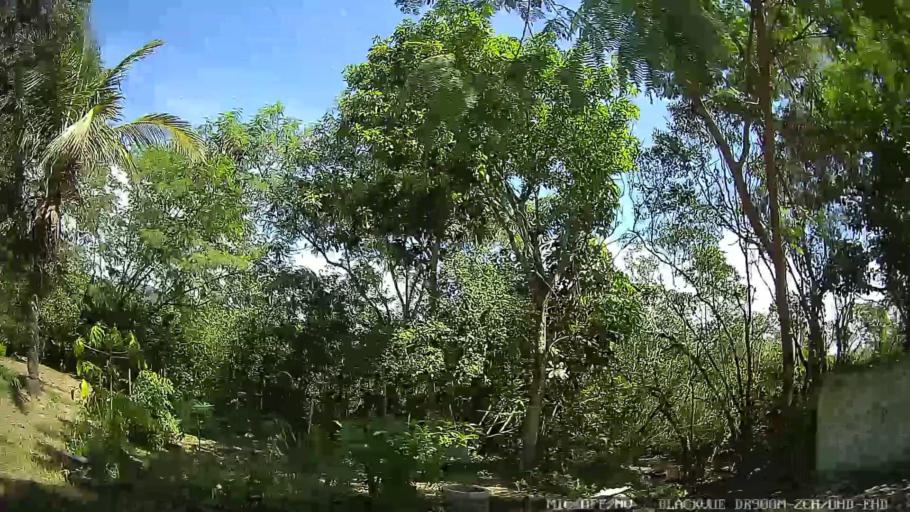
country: BR
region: Sao Paulo
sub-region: Peruibe
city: Peruibe
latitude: -24.3231
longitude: -47.0092
